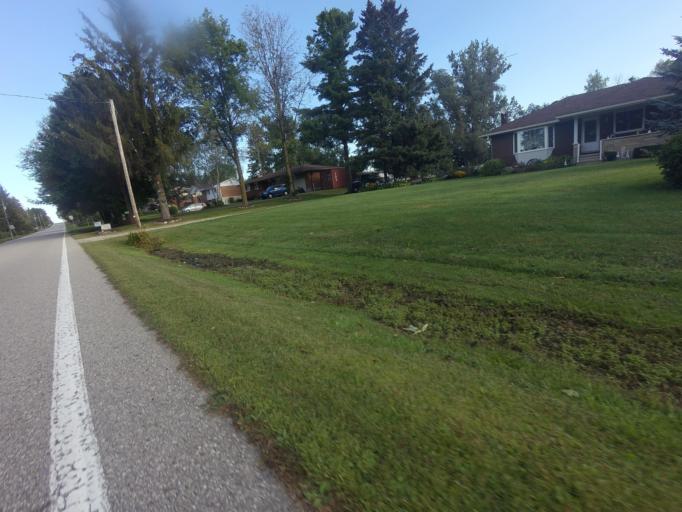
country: CA
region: Ontario
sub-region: Wellington County
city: Guelph
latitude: 43.5980
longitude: -80.3430
